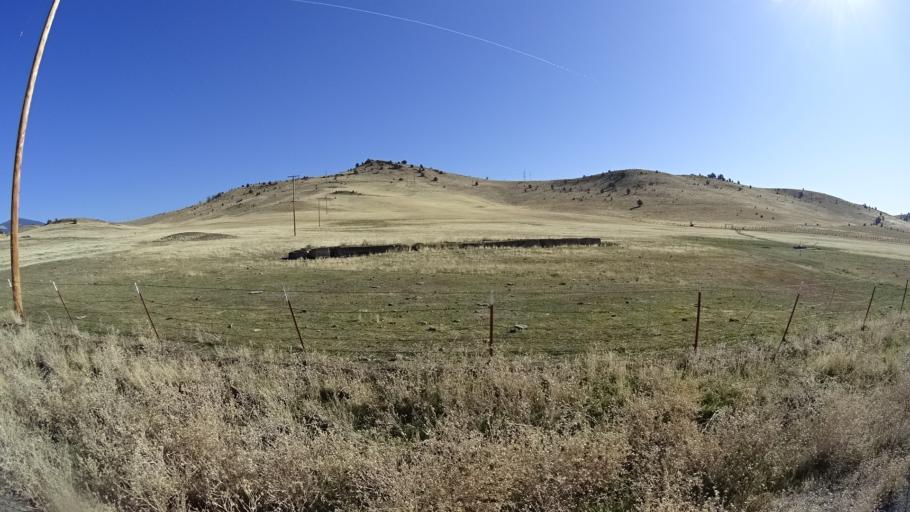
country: US
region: California
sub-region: Siskiyou County
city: Montague
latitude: 41.7440
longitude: -122.3654
